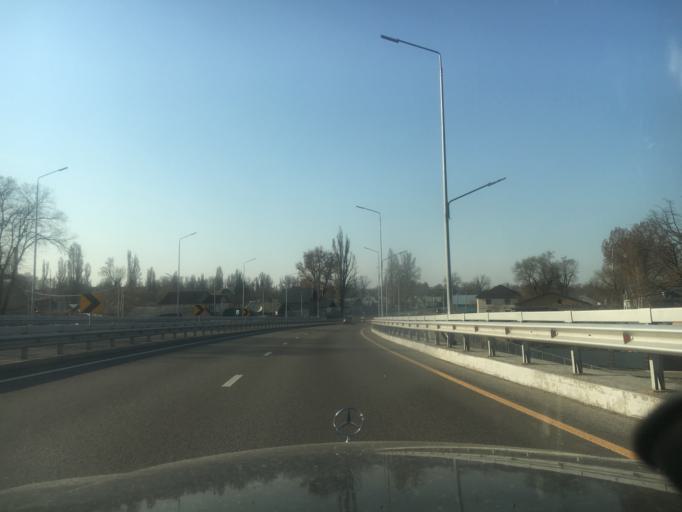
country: KZ
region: Almaty Qalasy
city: Almaty
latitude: 43.2775
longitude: 76.9418
